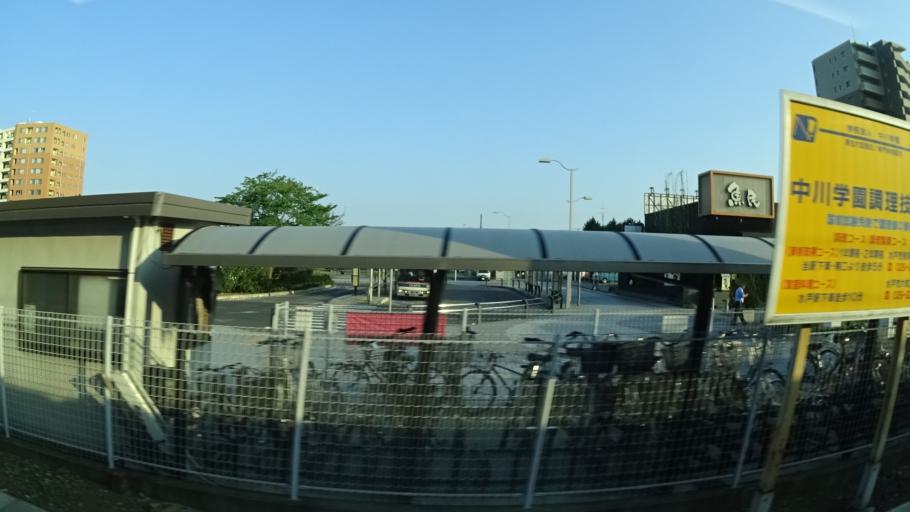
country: JP
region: Ibaraki
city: Mito-shi
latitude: 36.3817
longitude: 140.4150
